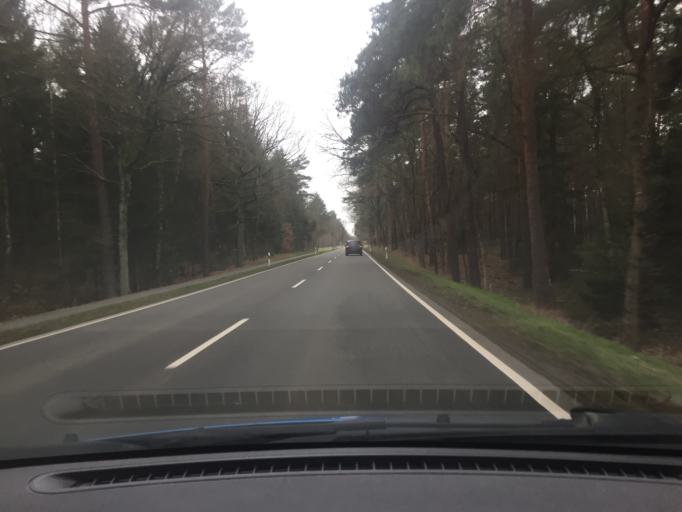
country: DE
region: Lower Saxony
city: Rosche
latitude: 52.9929
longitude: 10.7942
